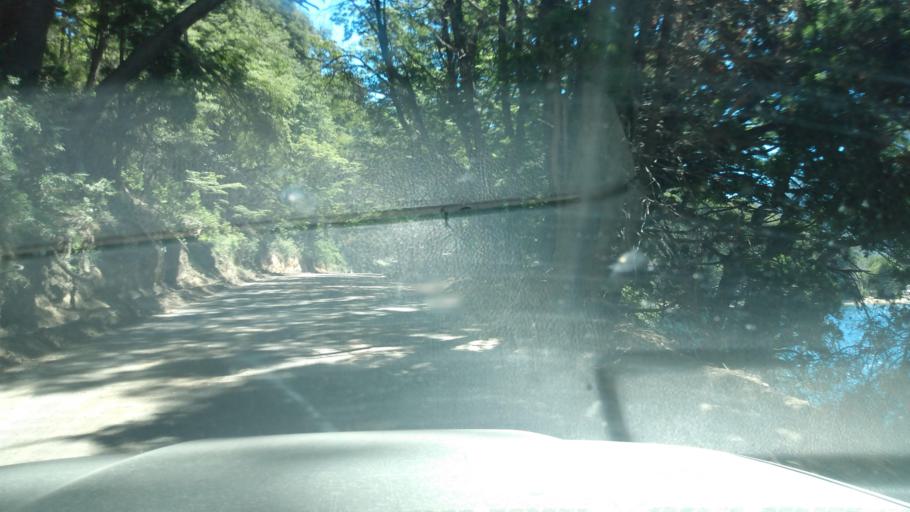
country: AR
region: Neuquen
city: Villa La Angostura
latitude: -40.6165
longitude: -71.5438
